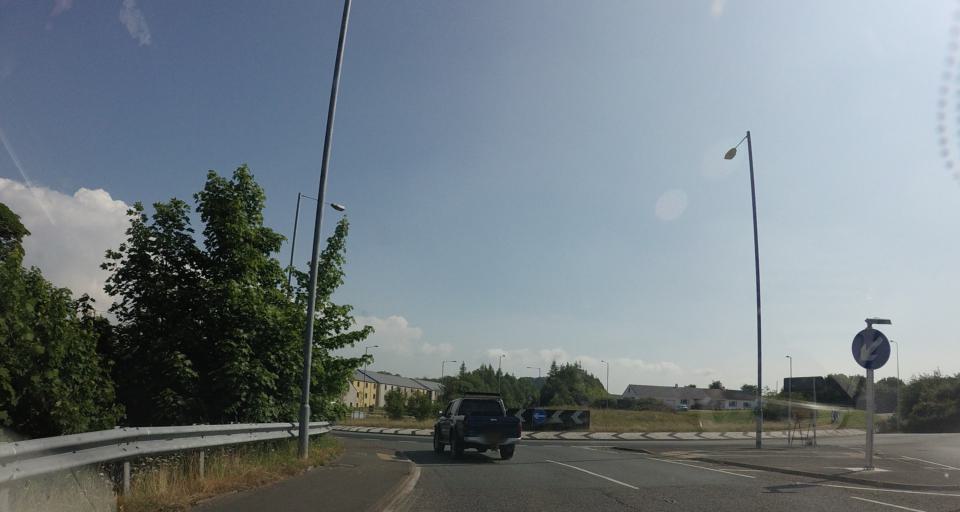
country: GB
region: England
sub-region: Cumbria
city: Cockermouth
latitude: 54.6534
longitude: -3.3724
